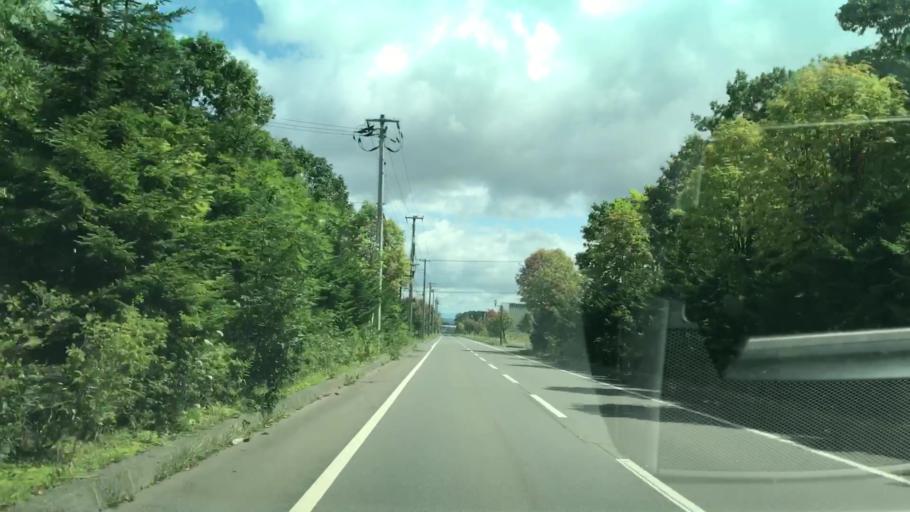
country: JP
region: Hokkaido
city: Chitose
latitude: 42.7776
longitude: 141.6086
